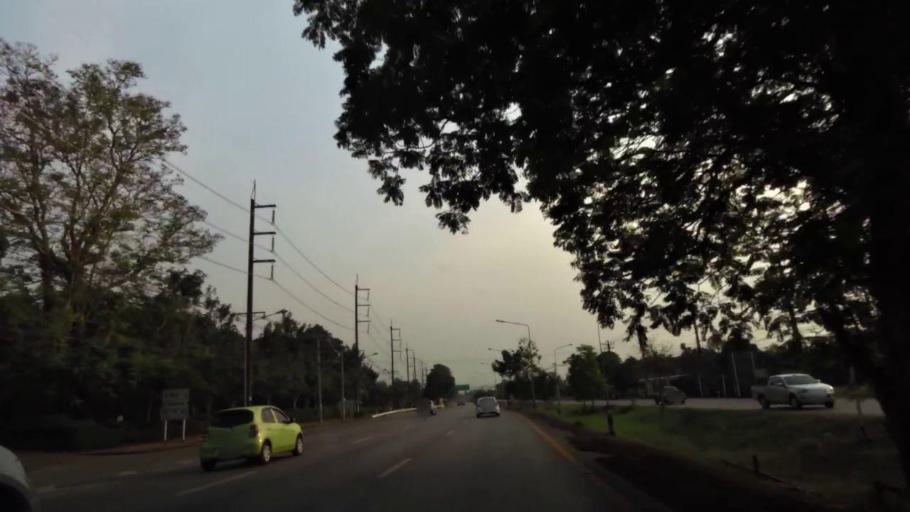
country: TH
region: Chanthaburi
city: Khlung
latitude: 12.5091
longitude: 102.1693
